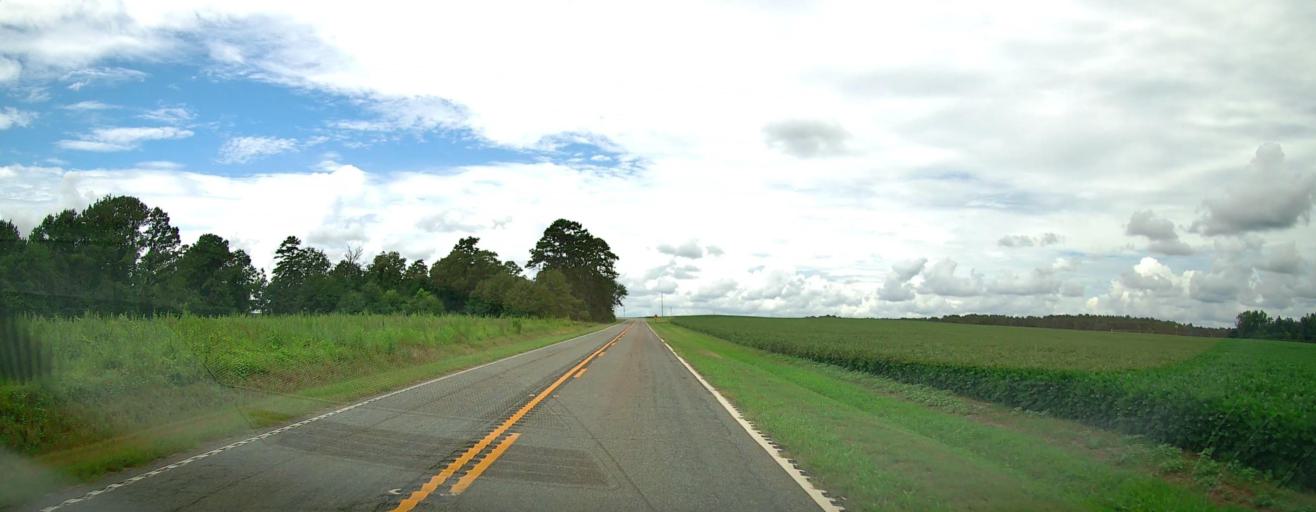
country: US
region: Georgia
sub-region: Dooly County
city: Unadilla
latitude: 32.2857
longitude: -83.8257
